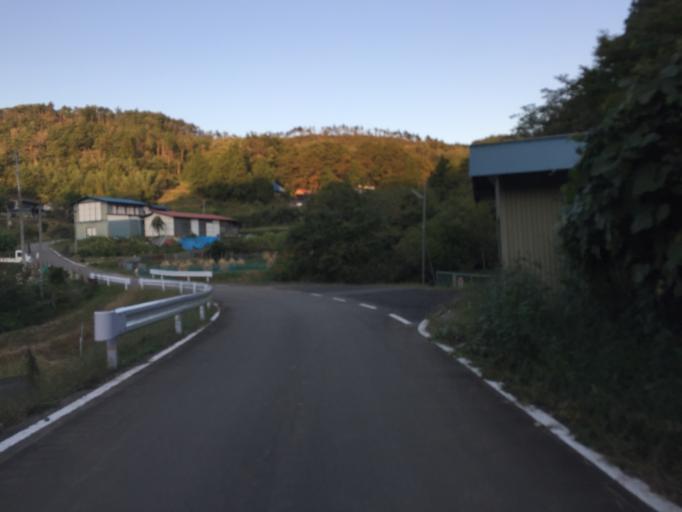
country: JP
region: Fukushima
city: Yanagawamachi-saiwaicho
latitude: 37.8420
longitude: 140.6333
